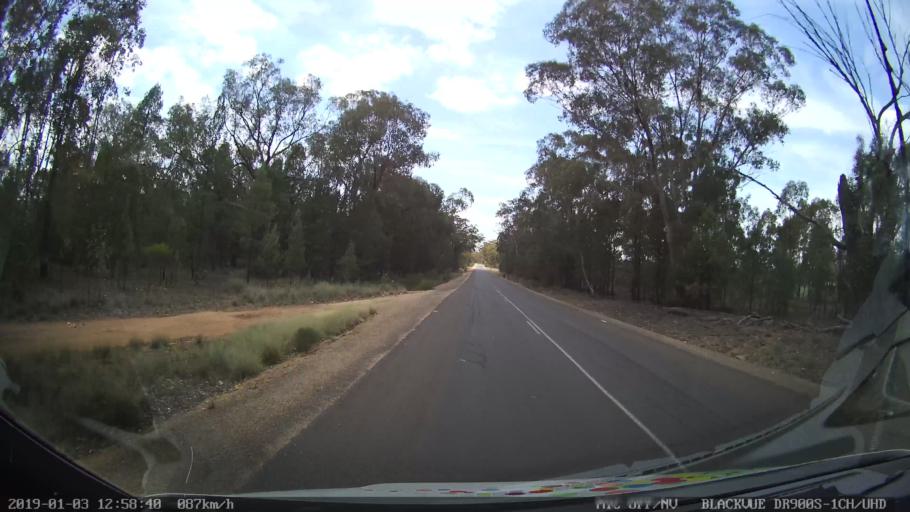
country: AU
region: New South Wales
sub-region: Cabonne
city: Canowindra
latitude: -33.6407
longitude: 148.3784
